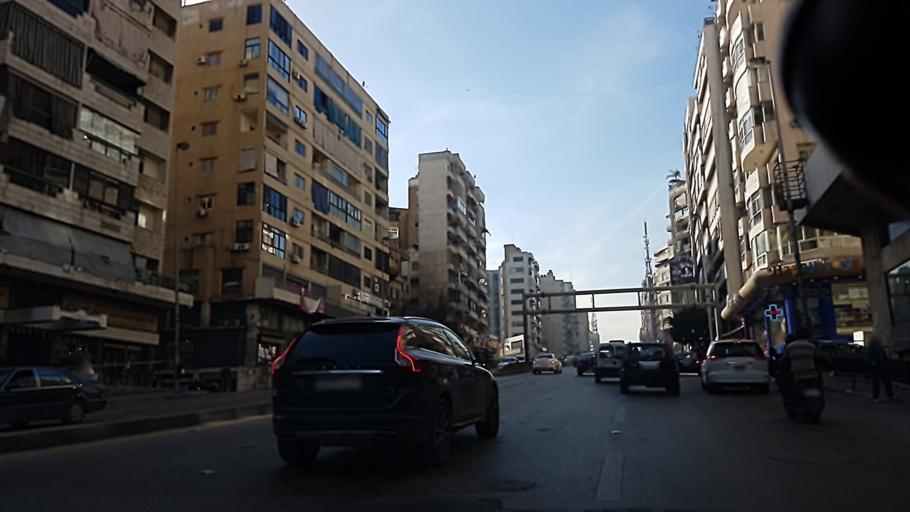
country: LB
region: Beyrouth
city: Beirut
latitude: 33.8903
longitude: 35.5002
